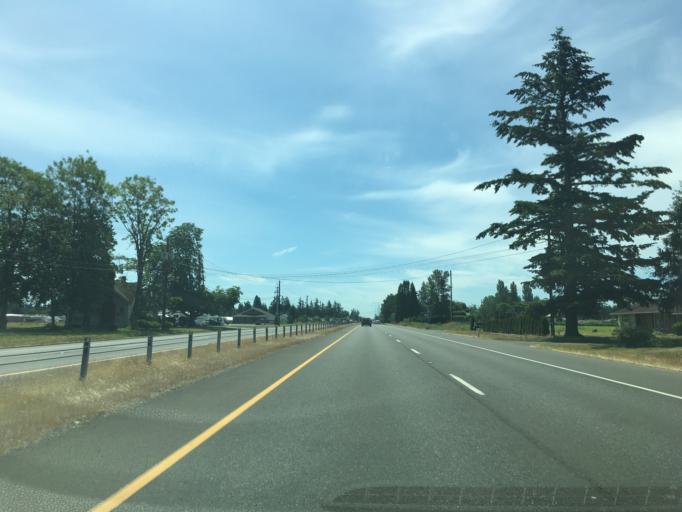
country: US
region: Washington
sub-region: Whatcom County
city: Lynden
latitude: 48.8970
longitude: -122.4855
